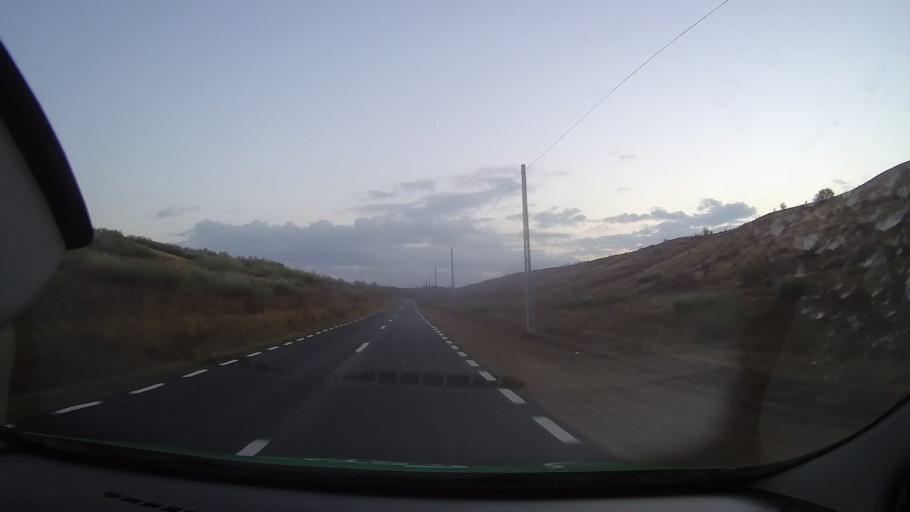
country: RO
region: Constanta
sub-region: Comuna Oltina
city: Oltina
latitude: 44.1423
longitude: 27.6658
